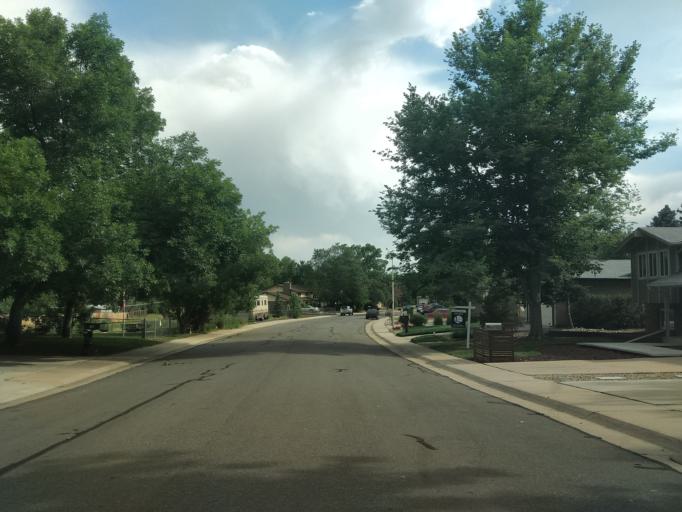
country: US
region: Colorado
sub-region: Jefferson County
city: Lakewood
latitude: 39.6998
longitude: -105.1089
